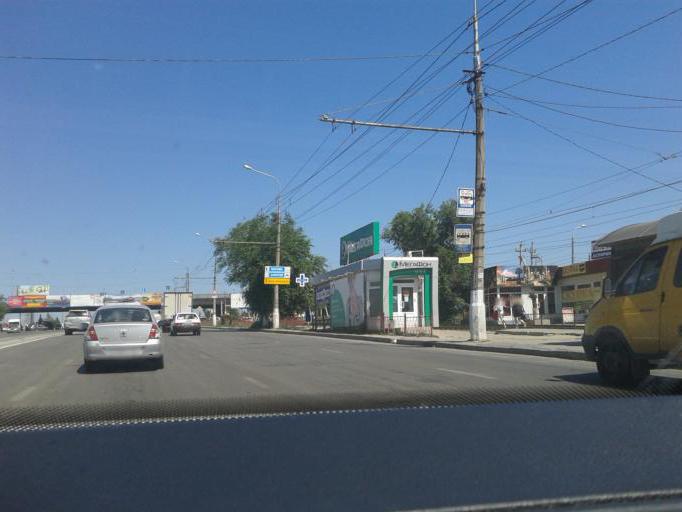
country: RU
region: Volgograd
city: Volgograd
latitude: 48.7523
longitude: 44.4835
